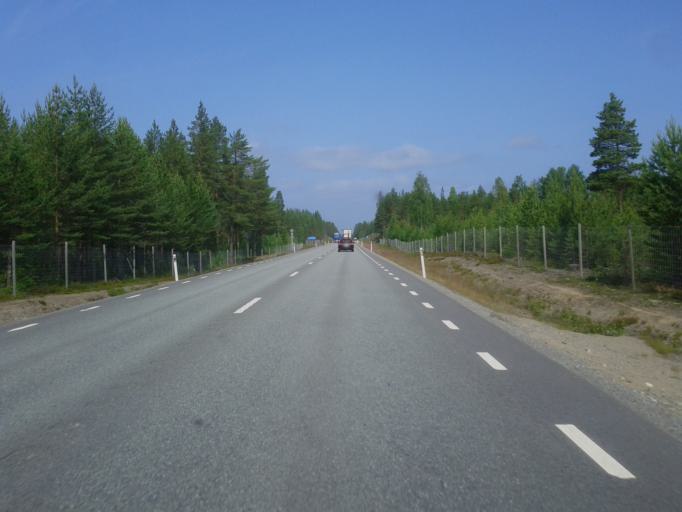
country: SE
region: Vaesterbotten
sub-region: Skelleftea Kommun
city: Burea
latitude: 64.5900
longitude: 21.2145
